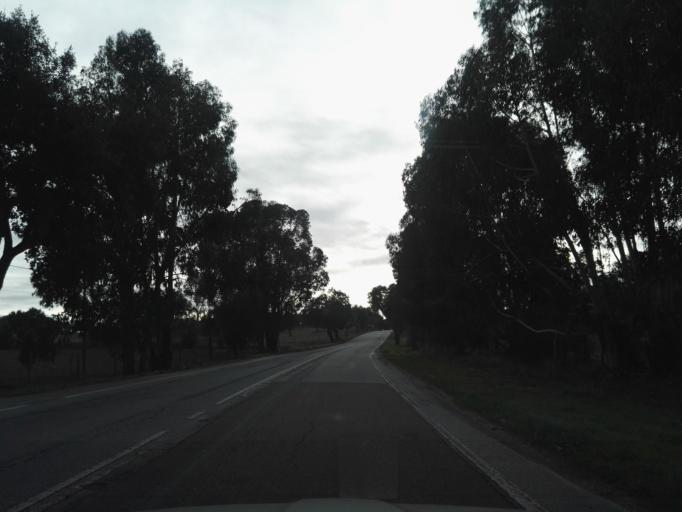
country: PT
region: Evora
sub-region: Redondo
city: Redondo
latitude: 38.6651
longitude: -7.5231
